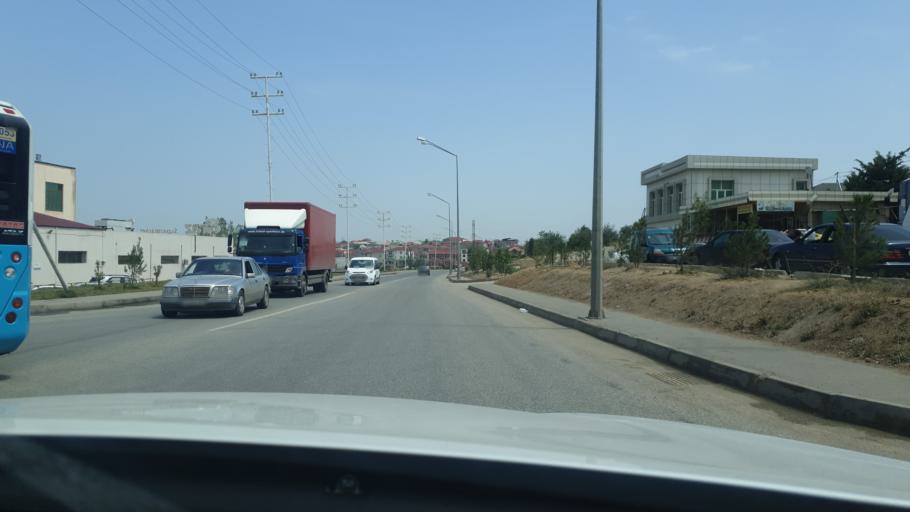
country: AZ
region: Baki
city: Qaracuxur
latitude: 40.3925
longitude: 49.9815
